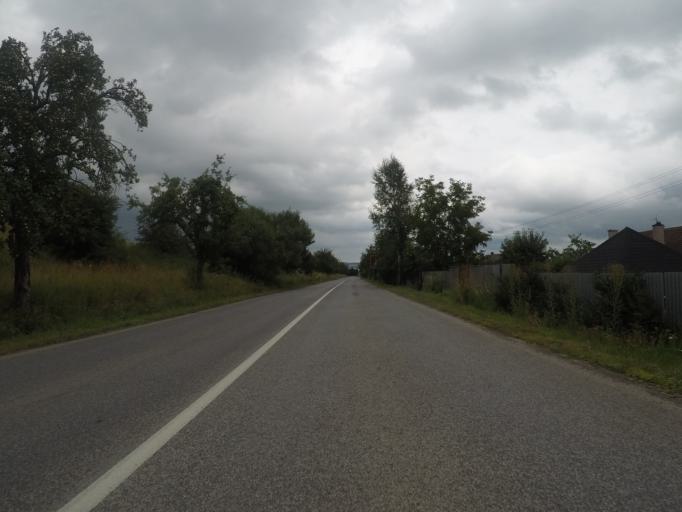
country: SK
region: Kosicky
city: Spisska Nova Ves
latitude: 48.9258
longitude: 20.5432
